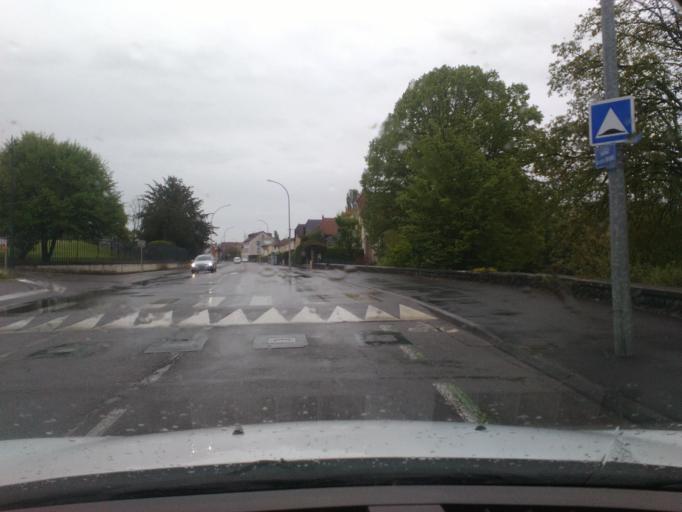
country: FR
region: Franche-Comte
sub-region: Departement de la Haute-Saone
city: Vesoul
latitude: 47.6245
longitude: 6.1639
